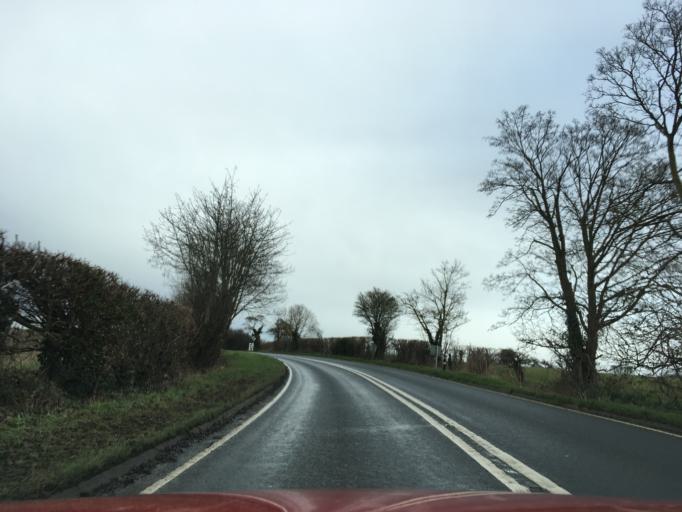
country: GB
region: England
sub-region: Worcestershire
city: Evesham
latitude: 52.0488
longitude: -1.9644
